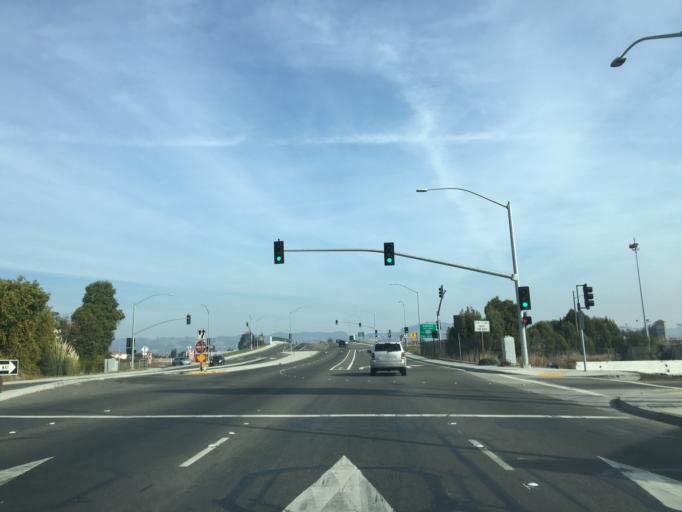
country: US
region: California
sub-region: Alameda County
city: San Leandro
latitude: 37.7091
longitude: -122.1697
